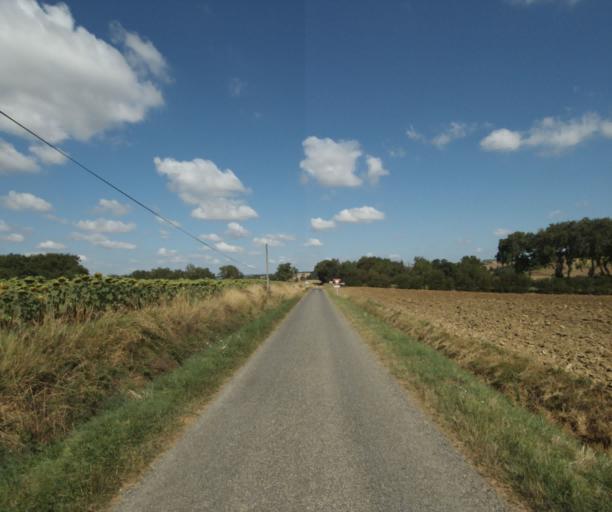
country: FR
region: Midi-Pyrenees
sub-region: Departement de la Haute-Garonne
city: Avignonet-Lauragais
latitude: 43.4428
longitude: 1.7899
